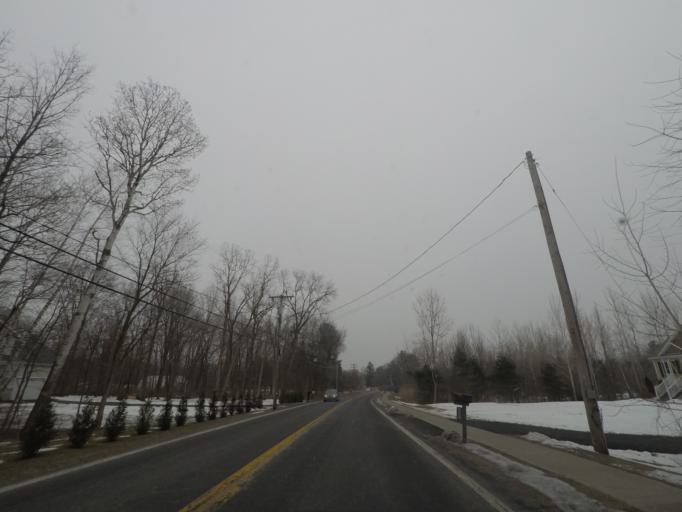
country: US
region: New York
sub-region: Rensselaer County
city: Castleton-on-Hudson
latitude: 42.5409
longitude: -73.8028
